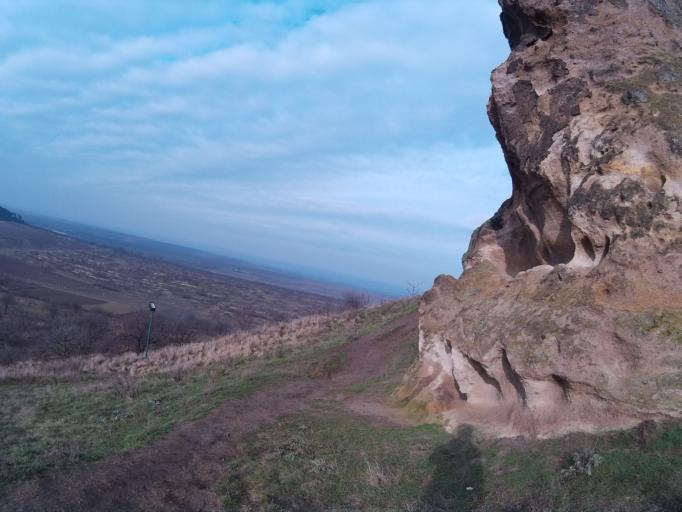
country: HU
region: Borsod-Abauj-Zemplen
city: Abaujszanto
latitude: 48.3438
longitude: 21.2326
